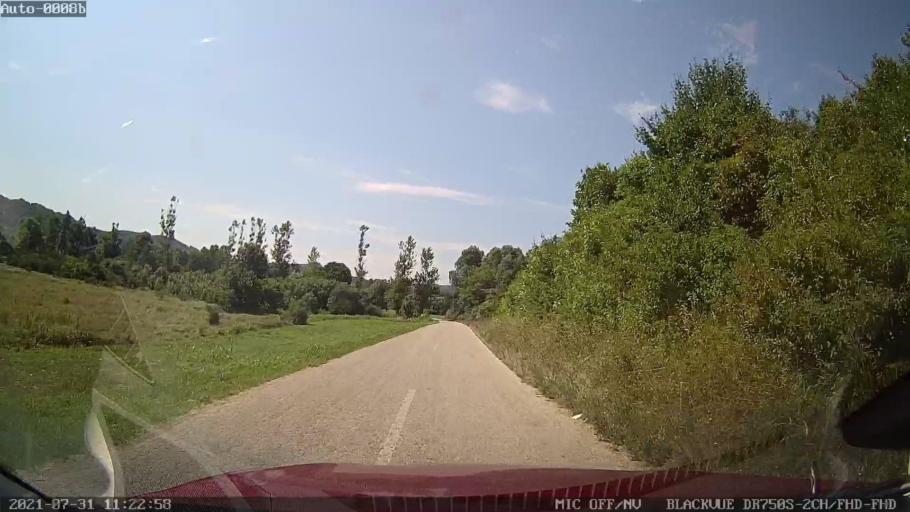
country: HR
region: Varazdinska
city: Jalzabet
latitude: 46.2196
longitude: 16.4651
